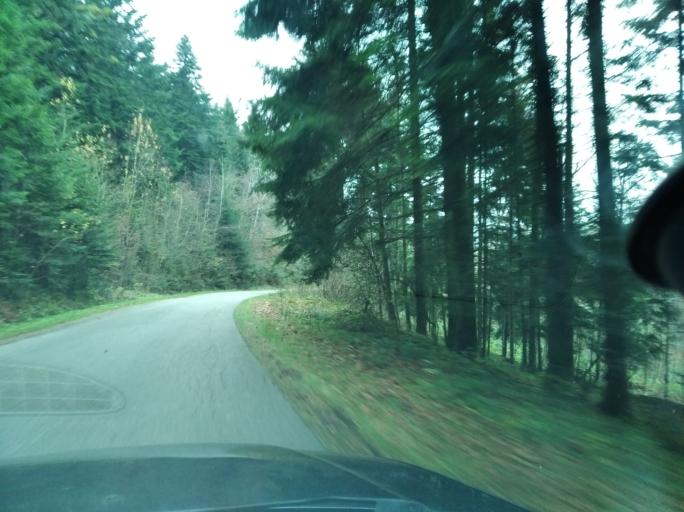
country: PL
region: Subcarpathian Voivodeship
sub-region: Powiat strzyzowski
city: Wysoka Strzyzowska
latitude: 49.8296
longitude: 21.7752
